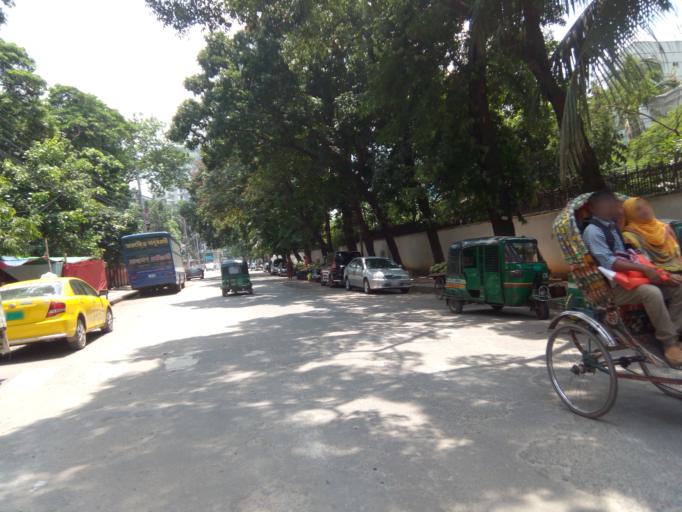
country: BD
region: Dhaka
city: Paltan
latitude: 23.7445
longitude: 90.3974
